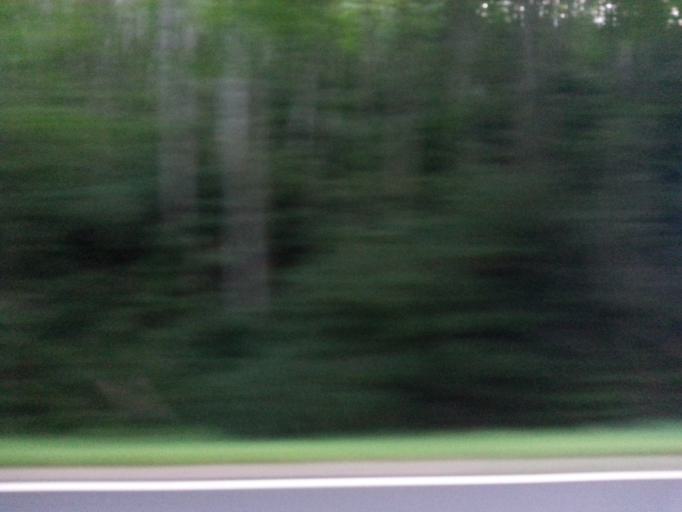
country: US
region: Tennessee
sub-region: Johnson County
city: Mountain City
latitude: 36.5748
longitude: -81.8472
